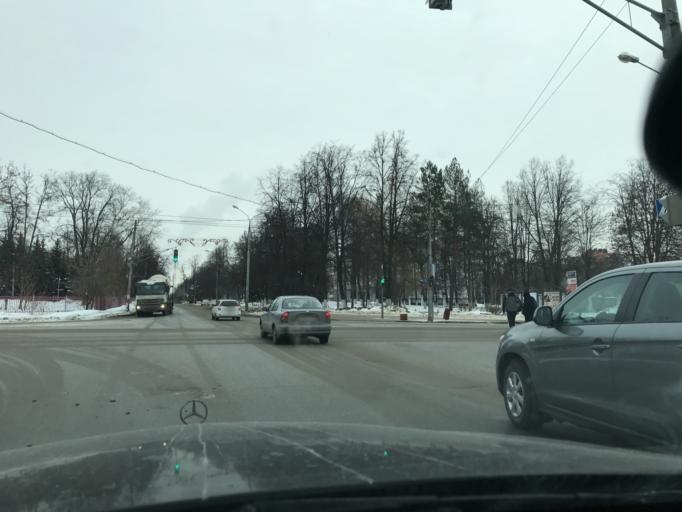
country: RU
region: Nizjnij Novgorod
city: Gorbatovka
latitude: 56.2463
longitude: 43.8501
